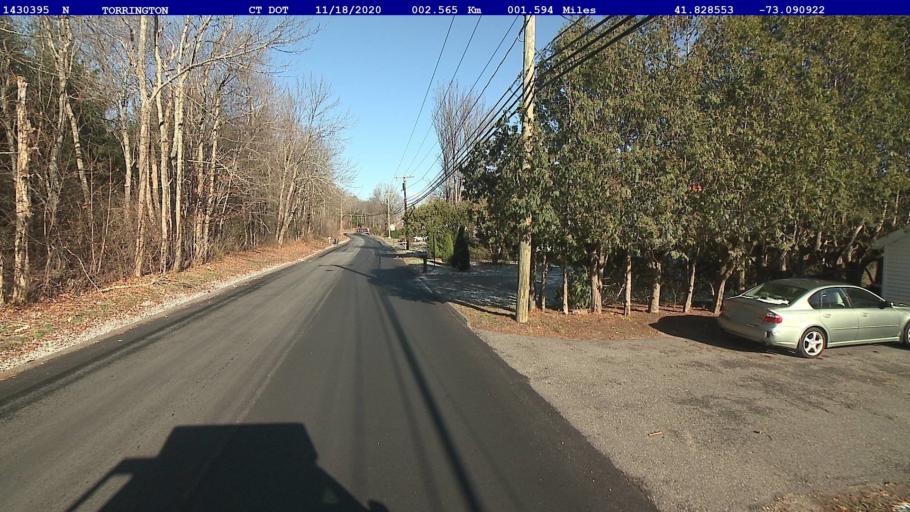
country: US
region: Connecticut
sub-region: Litchfield County
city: Torrington
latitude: 41.8286
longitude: -73.0909
